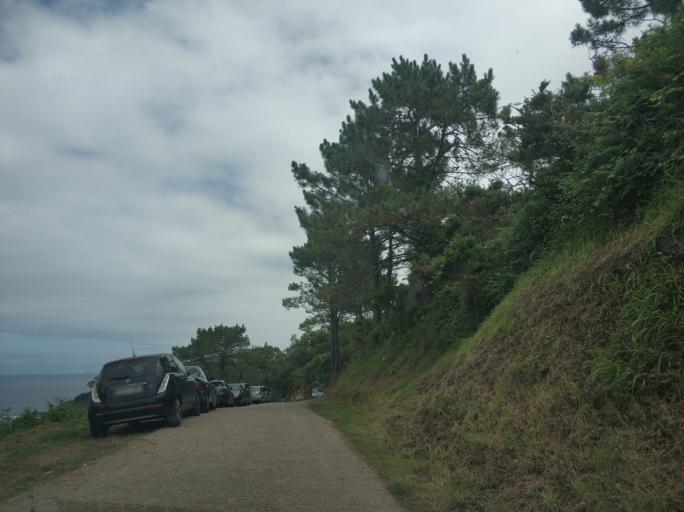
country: ES
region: Asturias
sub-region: Province of Asturias
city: Cudillero
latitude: 43.5653
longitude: -6.2954
